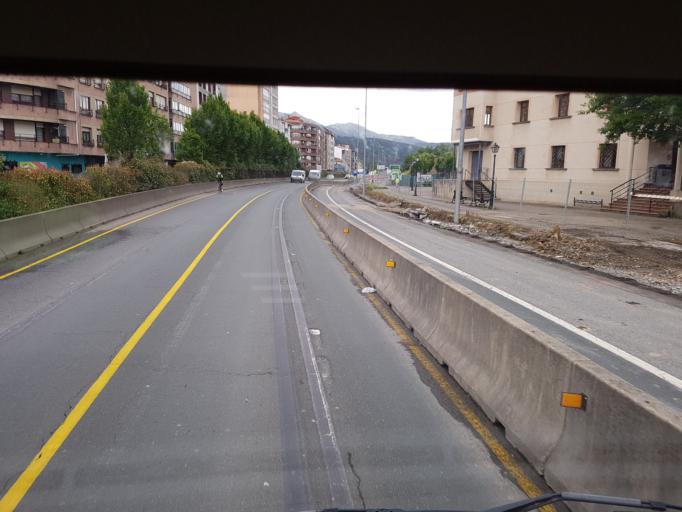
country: ES
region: Basque Country
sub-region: Bizkaia
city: Durango
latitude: 43.1752
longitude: -2.6352
